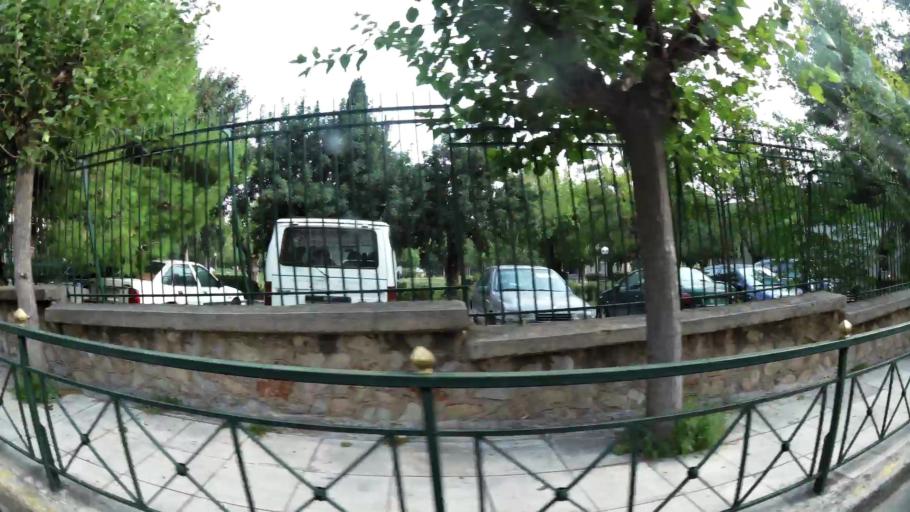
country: GR
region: Attica
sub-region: Nomarchia Athinas
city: Psychiko
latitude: 37.9965
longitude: 23.7655
